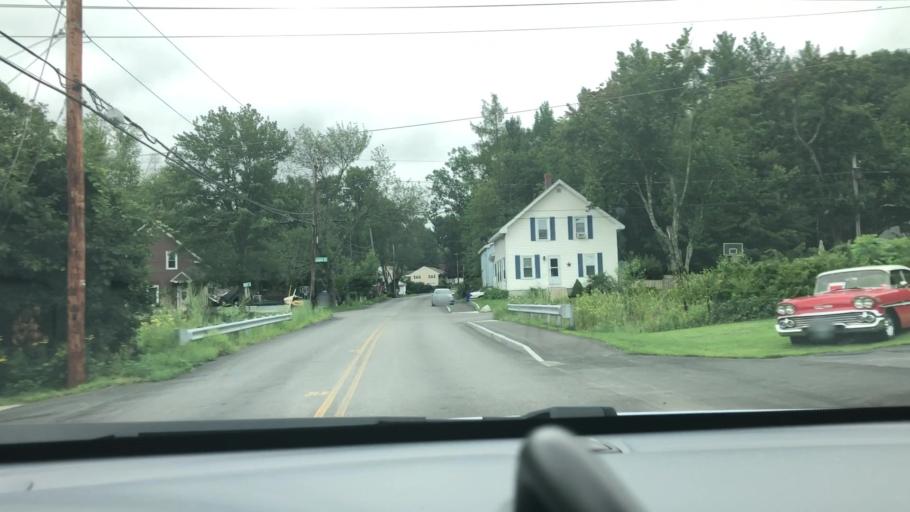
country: US
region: New Hampshire
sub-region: Hillsborough County
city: Pinardville
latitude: 42.9914
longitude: -71.5063
